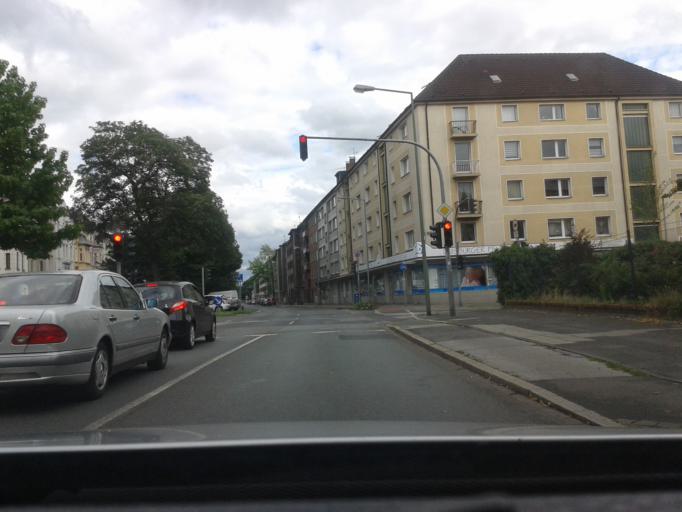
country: DE
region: North Rhine-Westphalia
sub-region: Regierungsbezirk Dusseldorf
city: Duisburg
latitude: 51.4194
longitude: 6.7865
